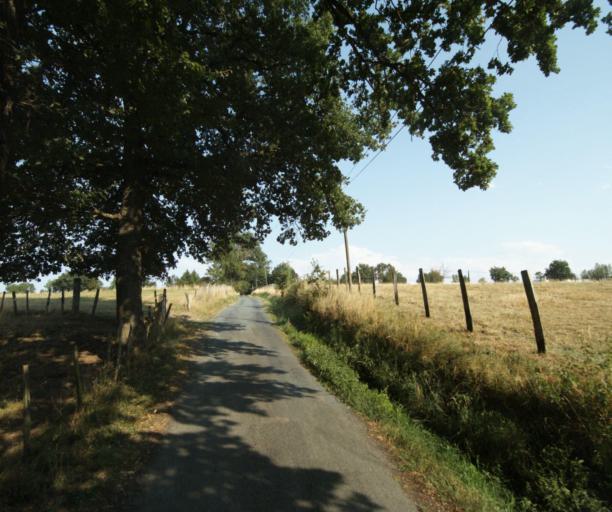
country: FR
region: Rhone-Alpes
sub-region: Departement du Rhone
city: Savigny
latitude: 45.8237
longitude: 4.5852
